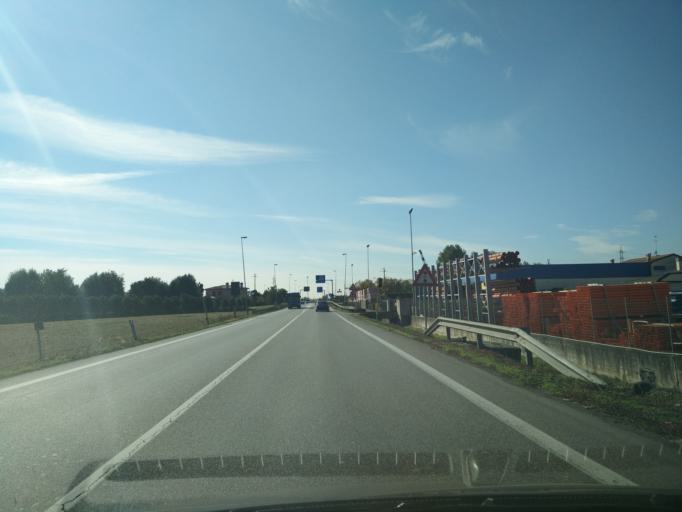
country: IT
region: Veneto
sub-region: Provincia di Venezia
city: Fornase
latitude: 45.4369
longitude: 12.1952
